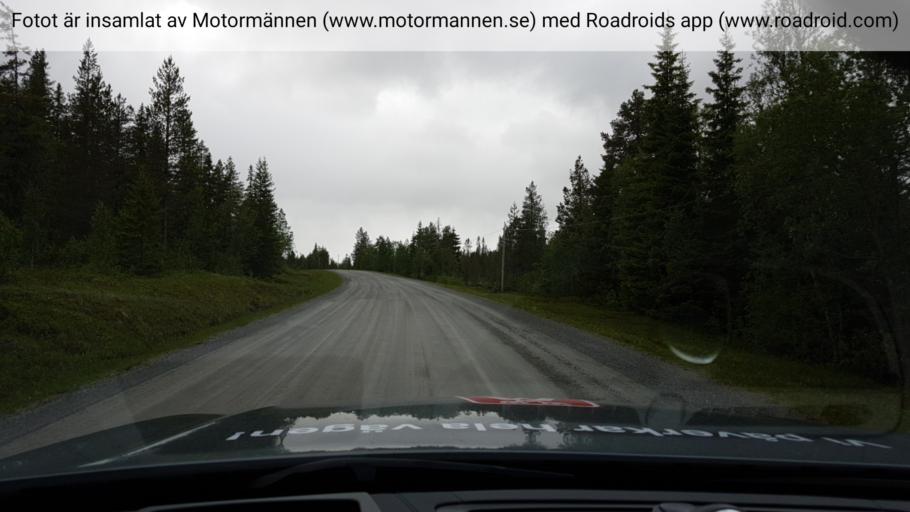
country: NO
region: Nord-Trondelag
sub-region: Snasa
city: Snaase
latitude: 63.7244
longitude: 12.6021
